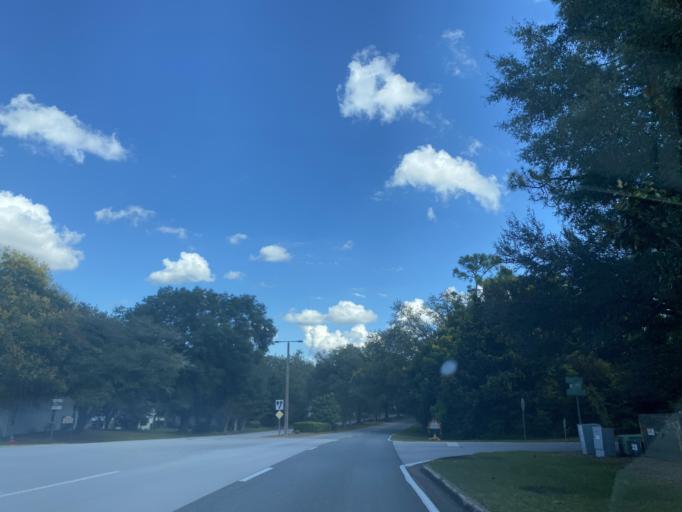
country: US
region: Florida
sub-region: Marion County
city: Ocala
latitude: 29.0571
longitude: -82.2571
